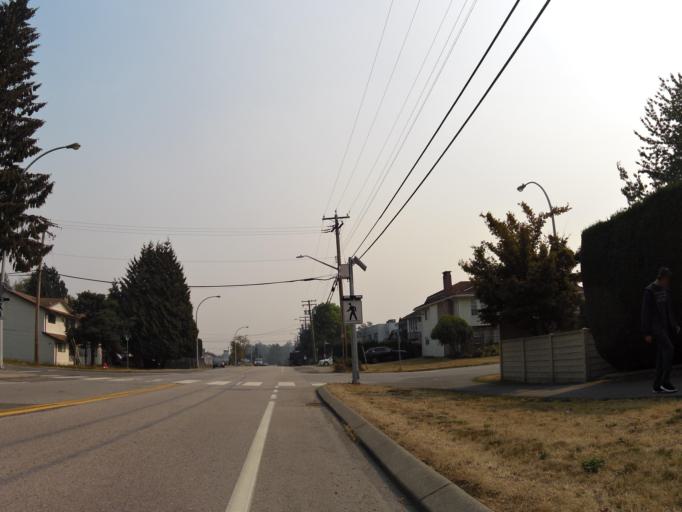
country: CA
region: British Columbia
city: Delta
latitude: 49.1558
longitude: -122.8828
